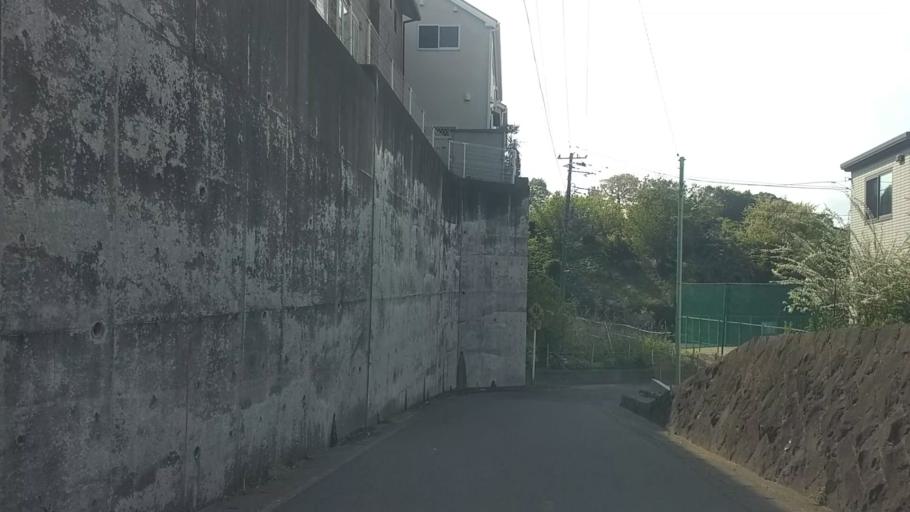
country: JP
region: Kanagawa
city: Kamakura
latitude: 35.3786
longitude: 139.5643
